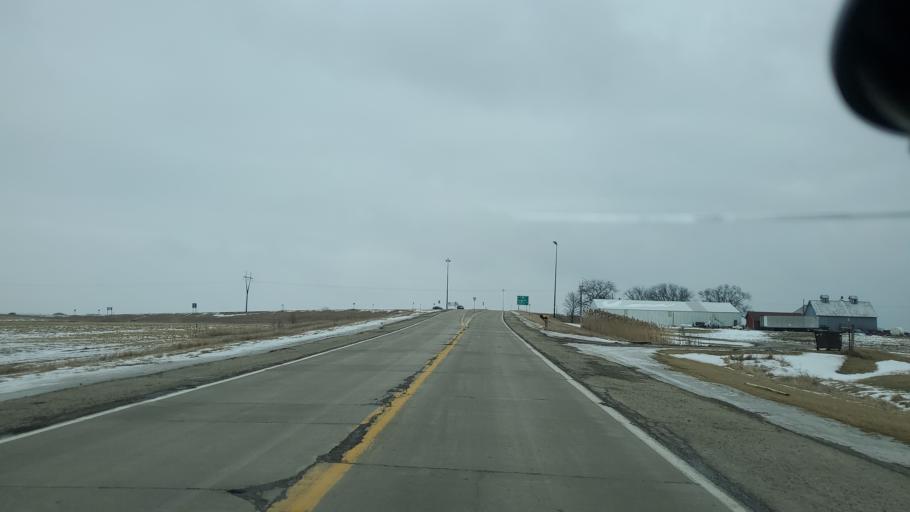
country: US
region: Illinois
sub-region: Marshall County
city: Wenona
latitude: 41.1190
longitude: -89.0807
